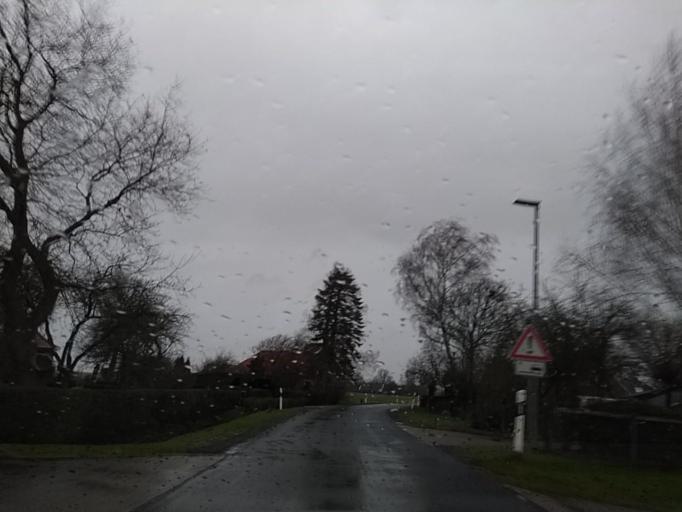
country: DE
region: Lower Saxony
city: Bunde
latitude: 53.2820
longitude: 7.2670
